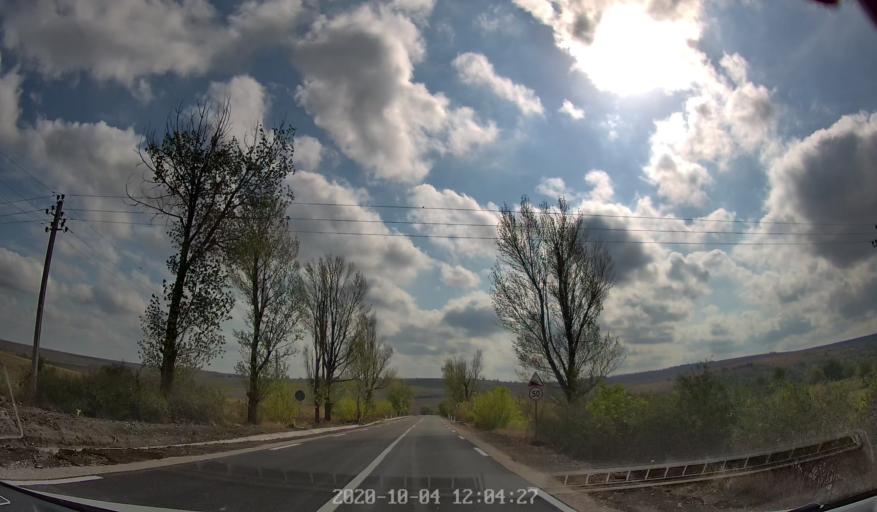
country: MD
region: Rezina
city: Saharna
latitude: 47.6037
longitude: 28.9430
